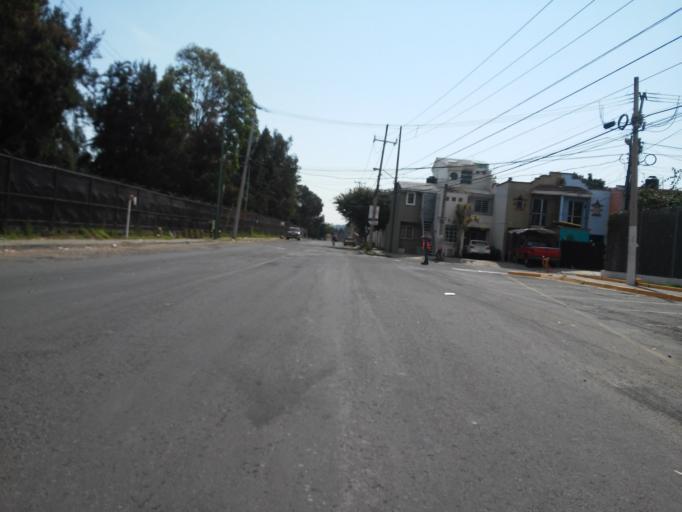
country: MX
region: Jalisco
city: Guadalajara
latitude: 20.6447
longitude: -103.4173
